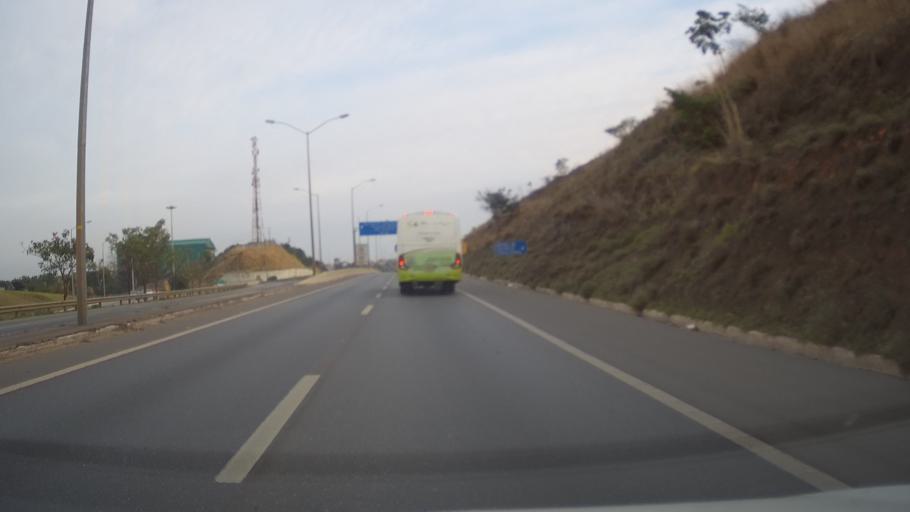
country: BR
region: Minas Gerais
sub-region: Vespasiano
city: Vespasiano
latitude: -19.7622
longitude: -43.9479
